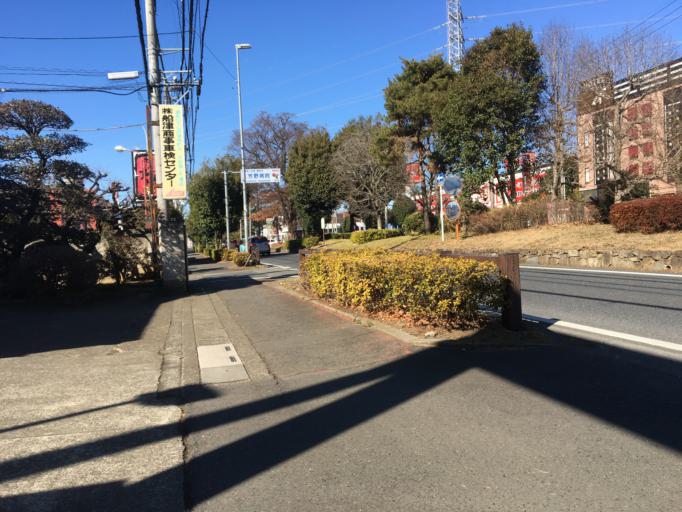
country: JP
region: Saitama
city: Oi
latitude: 35.8425
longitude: 139.5228
